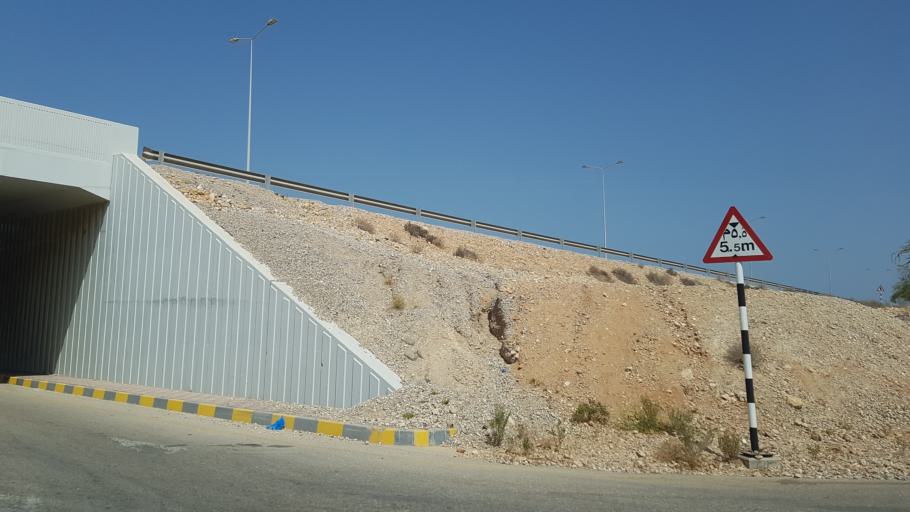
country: OM
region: Ash Sharqiyah
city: Sur
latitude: 22.8445
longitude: 59.2405
